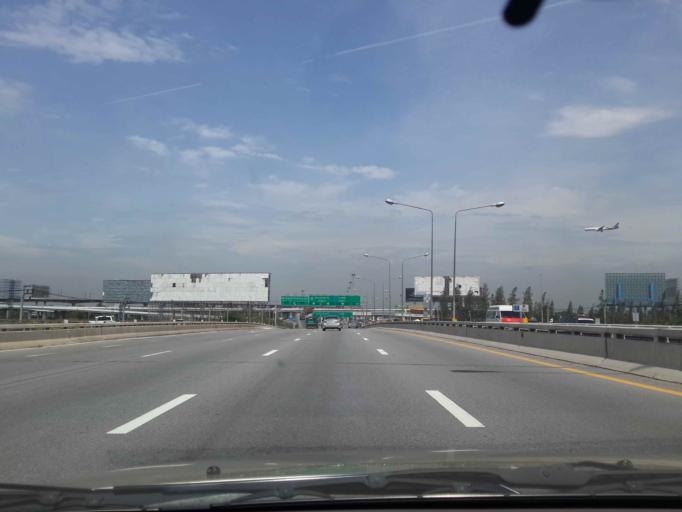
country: TH
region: Bangkok
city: Lat Krabang
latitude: 13.7315
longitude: 100.7646
